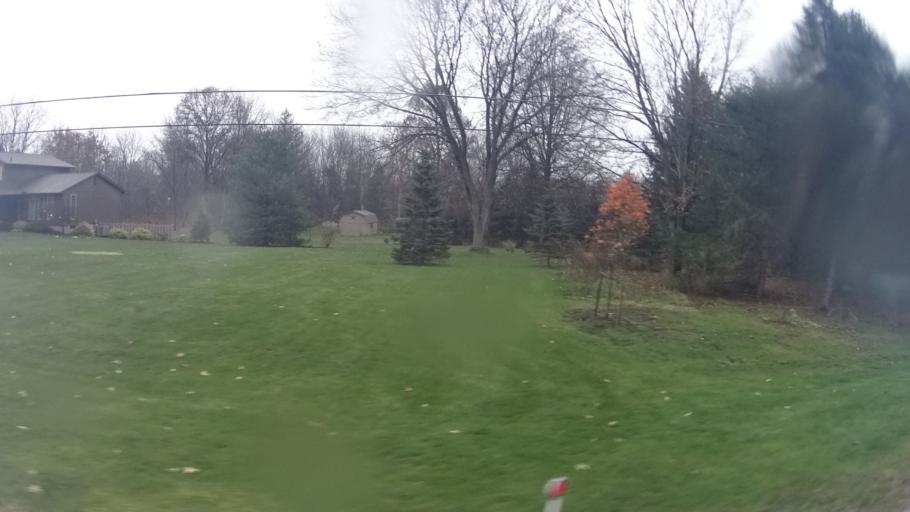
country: US
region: Ohio
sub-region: Lorain County
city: Lagrange
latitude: 41.2751
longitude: -82.1333
